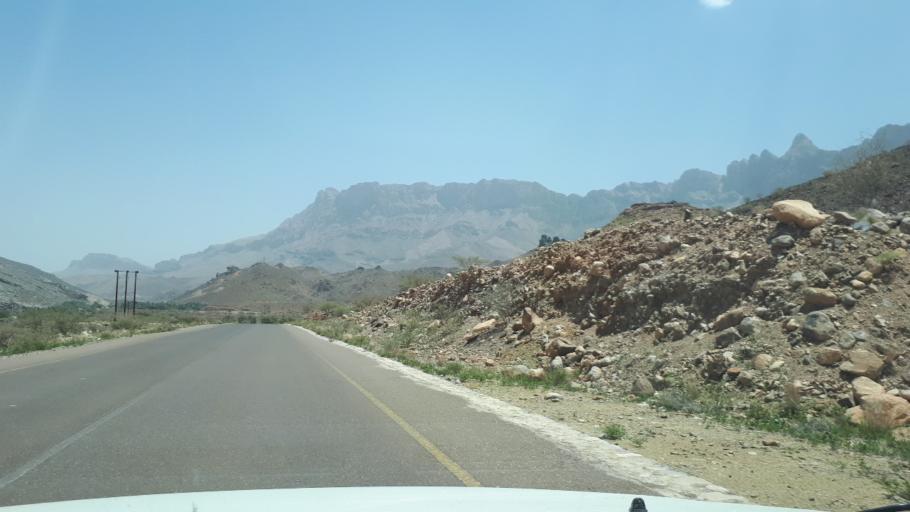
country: OM
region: Muhafazat ad Dakhiliyah
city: Bahla'
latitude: 23.1796
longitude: 57.1430
